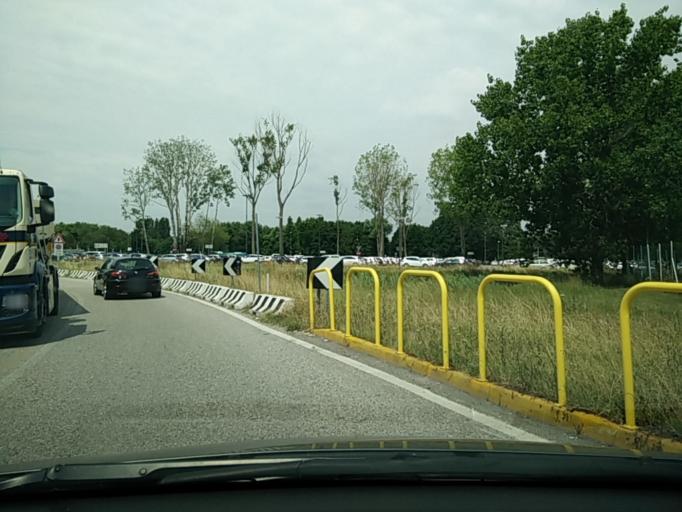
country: IT
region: Veneto
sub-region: Provincia di Venezia
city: Tessera
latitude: 45.5051
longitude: 12.3378
